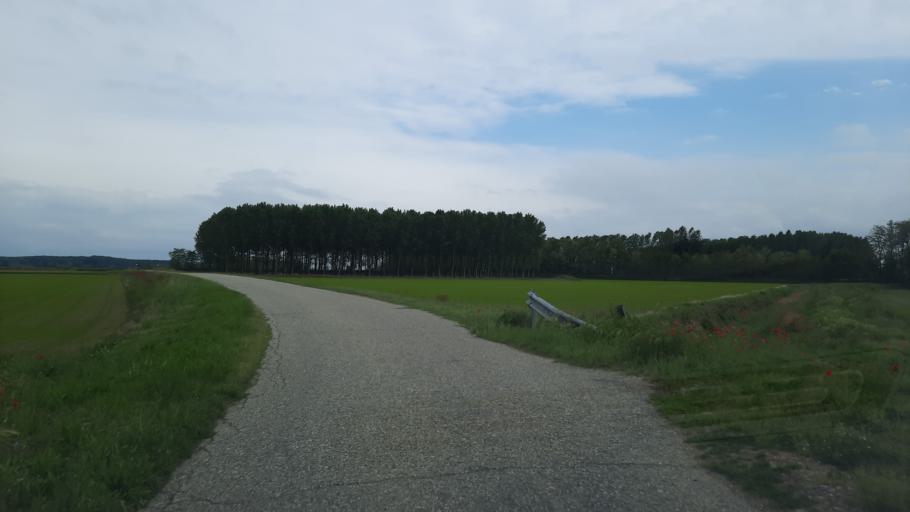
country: IT
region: Lombardy
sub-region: Provincia di Pavia
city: Cozzo
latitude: 45.2217
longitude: 8.6050
